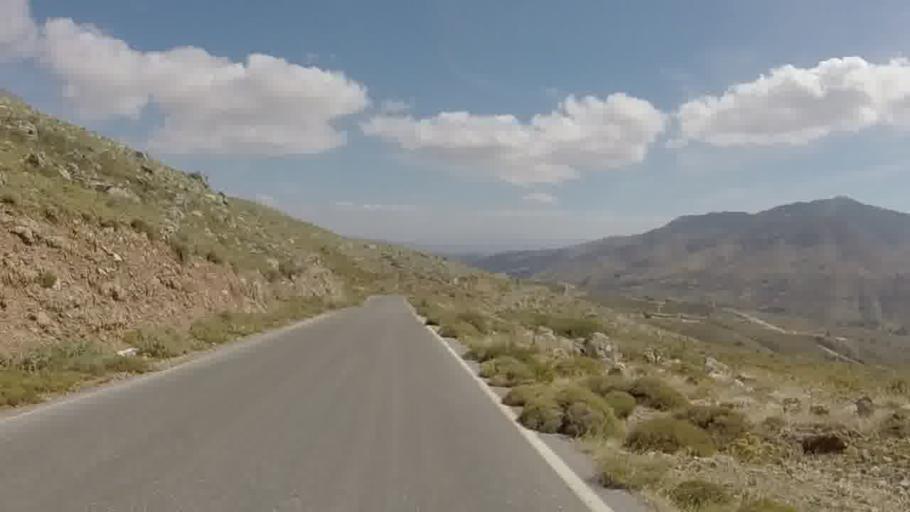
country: GR
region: Crete
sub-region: Nomos Rethymnis
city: Agia Galini
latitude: 35.1573
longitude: 24.6151
